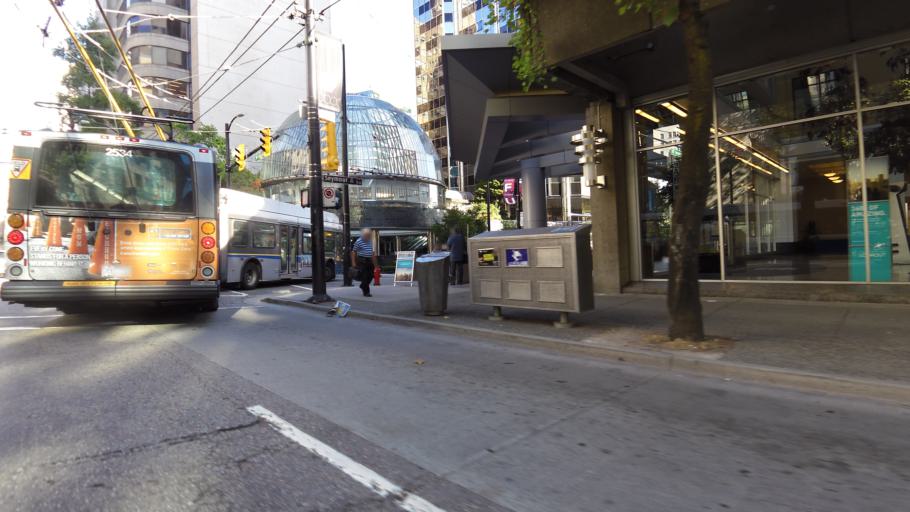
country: CA
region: British Columbia
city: West End
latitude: 49.2846
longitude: -123.1127
